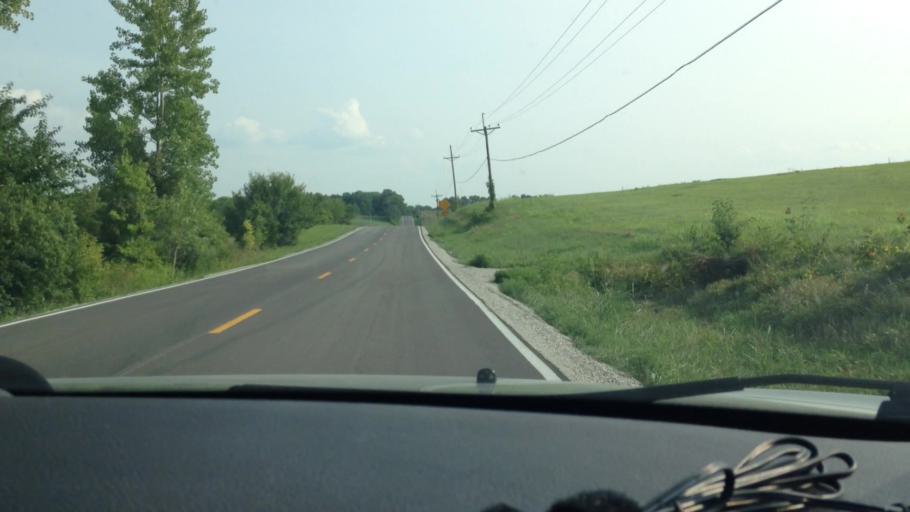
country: US
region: Missouri
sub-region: Platte County
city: Platte City
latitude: 39.3965
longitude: -94.7797
